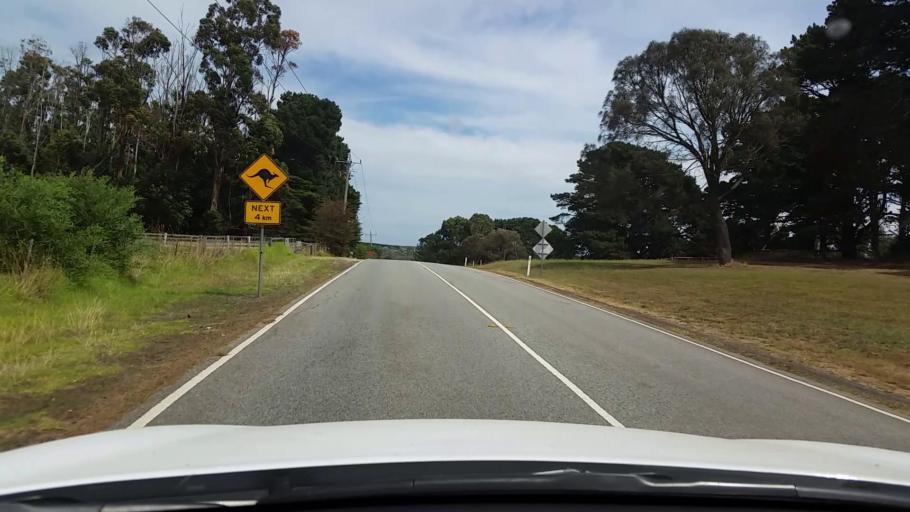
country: AU
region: Victoria
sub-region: Mornington Peninsula
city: Rosebud
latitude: -38.4780
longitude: 144.9427
